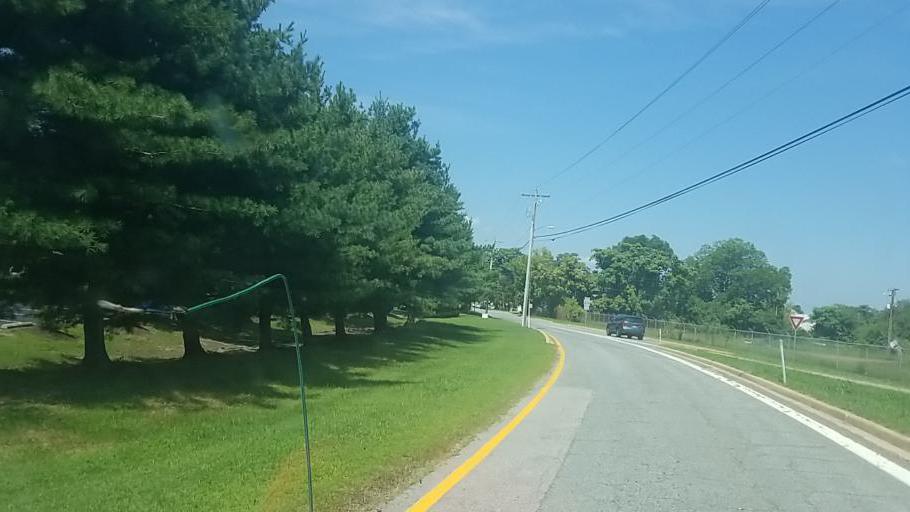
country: US
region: Maryland
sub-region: Caroline County
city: Denton
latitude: 38.8845
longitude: -75.8218
